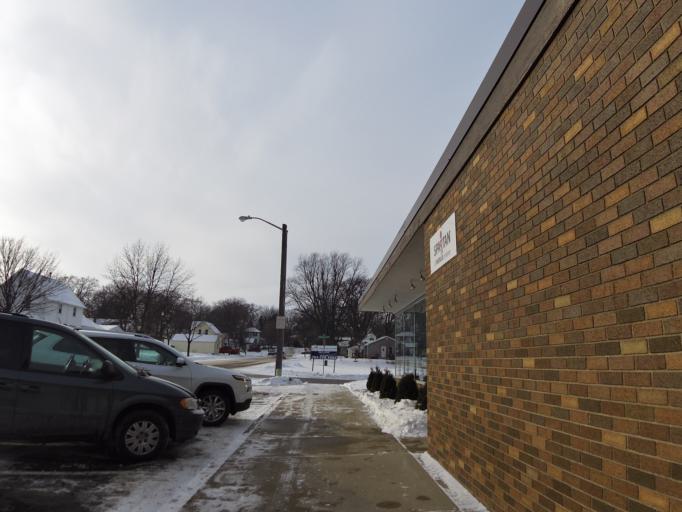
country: US
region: Minnesota
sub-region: McLeod County
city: Hutchinson
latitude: 44.8935
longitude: -94.3703
